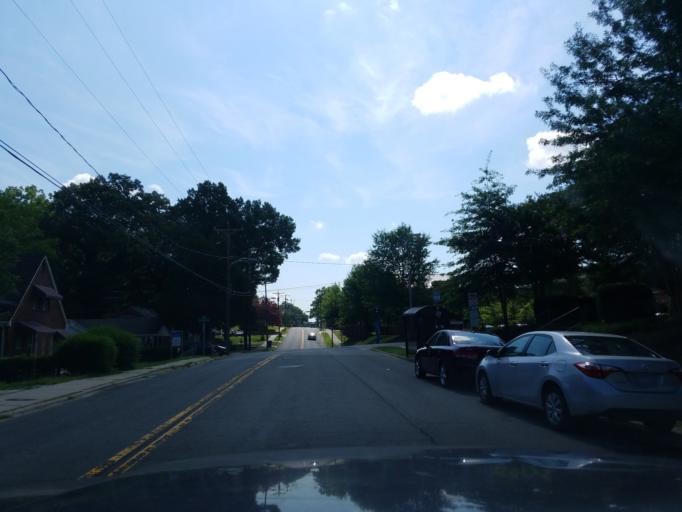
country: US
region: North Carolina
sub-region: Durham County
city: Durham
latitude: 35.9764
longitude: -78.9033
